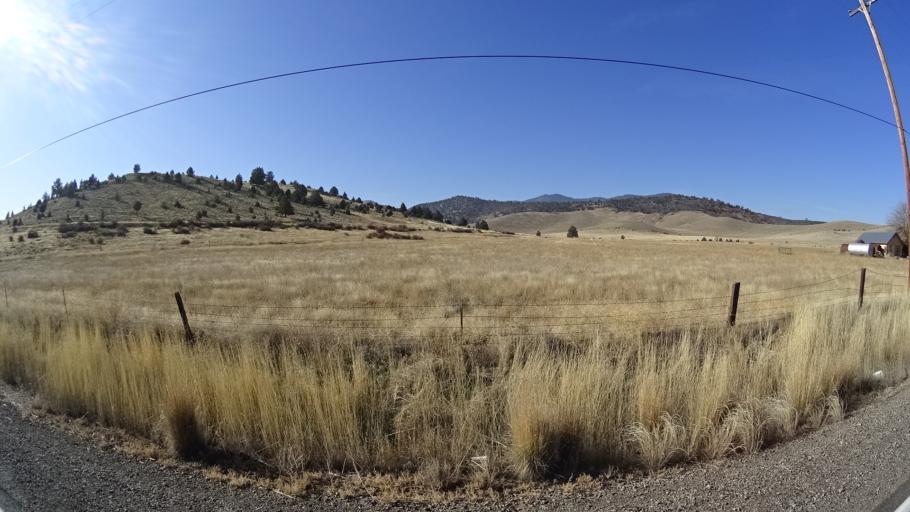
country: US
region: California
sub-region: Siskiyou County
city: Montague
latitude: 41.6439
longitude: -122.5358
